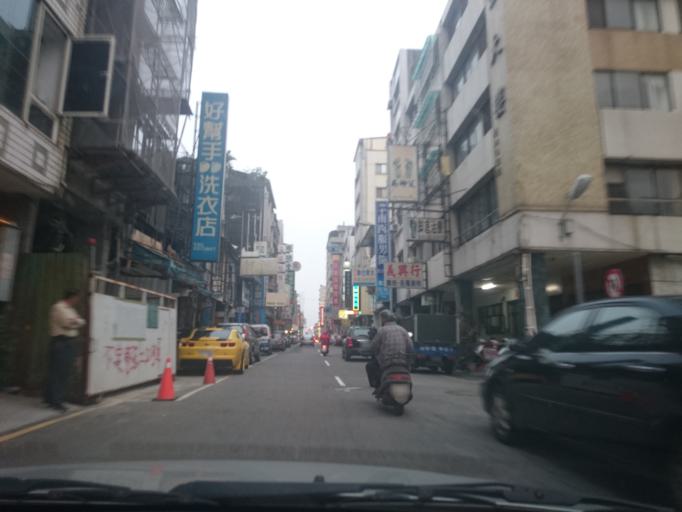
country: TW
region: Taiwan
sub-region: Taichung City
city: Taichung
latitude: 24.1469
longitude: 120.6759
